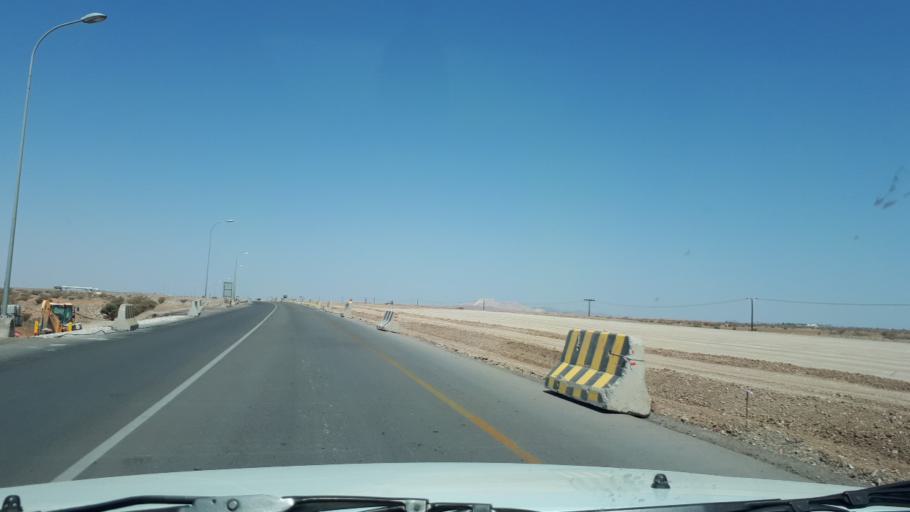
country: OM
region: Ash Sharqiyah
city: Badiyah
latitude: 22.4951
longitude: 58.9619
